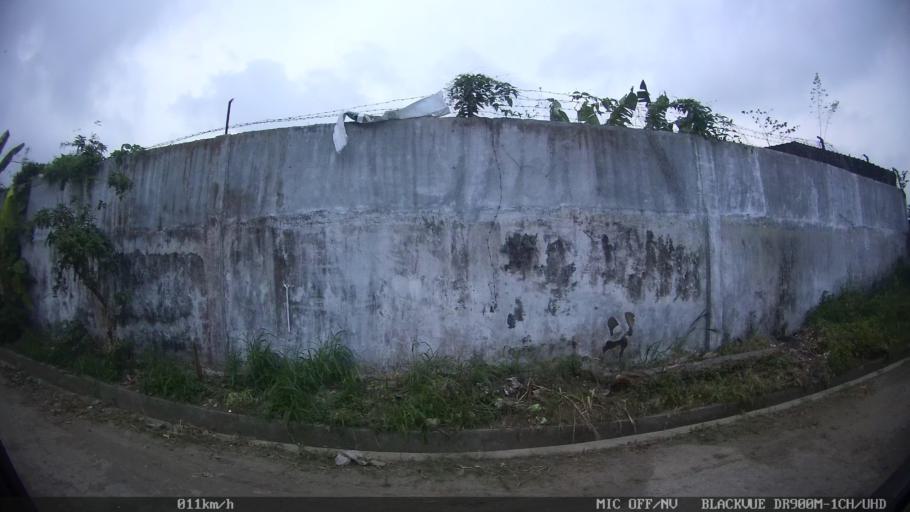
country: ID
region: Lampung
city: Bandarlampung
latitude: -5.4059
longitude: 105.2799
